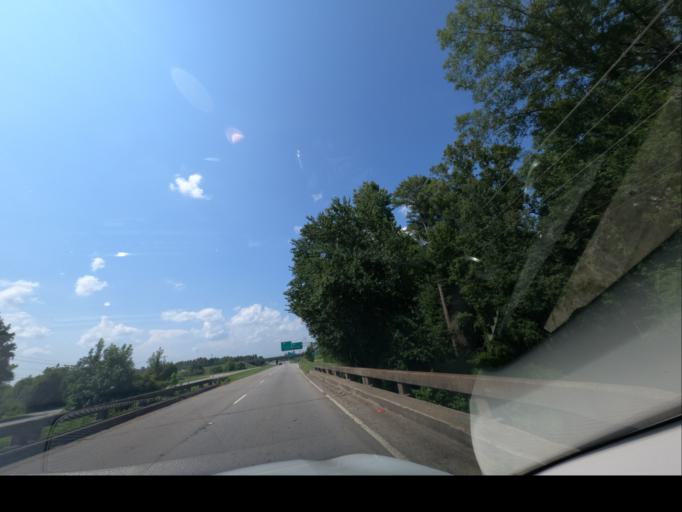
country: US
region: South Carolina
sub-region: Richland County
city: Columbia
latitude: 33.9481
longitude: -80.9888
